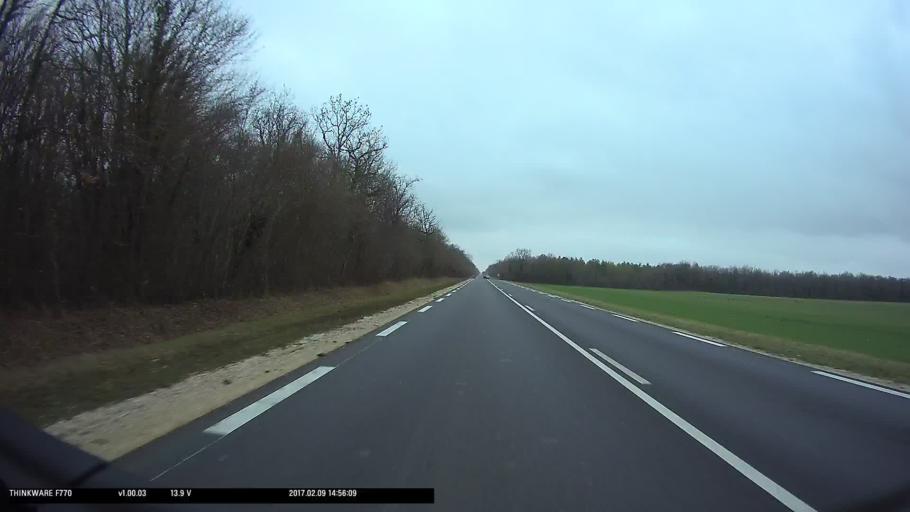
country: FR
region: Centre
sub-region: Departement du Cher
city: Levet
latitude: 46.8699
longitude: 2.4182
